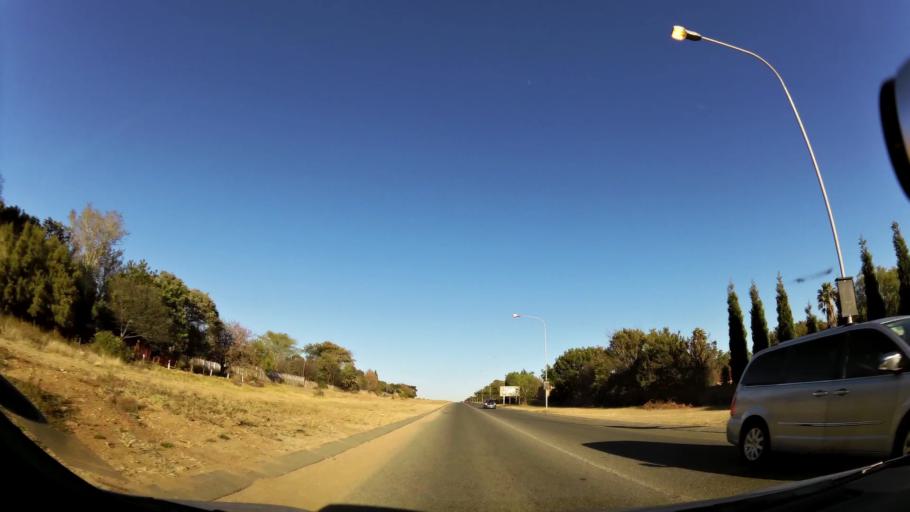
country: ZA
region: Gauteng
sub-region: City of Tshwane Metropolitan Municipality
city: Centurion
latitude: -25.8991
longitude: 28.1422
